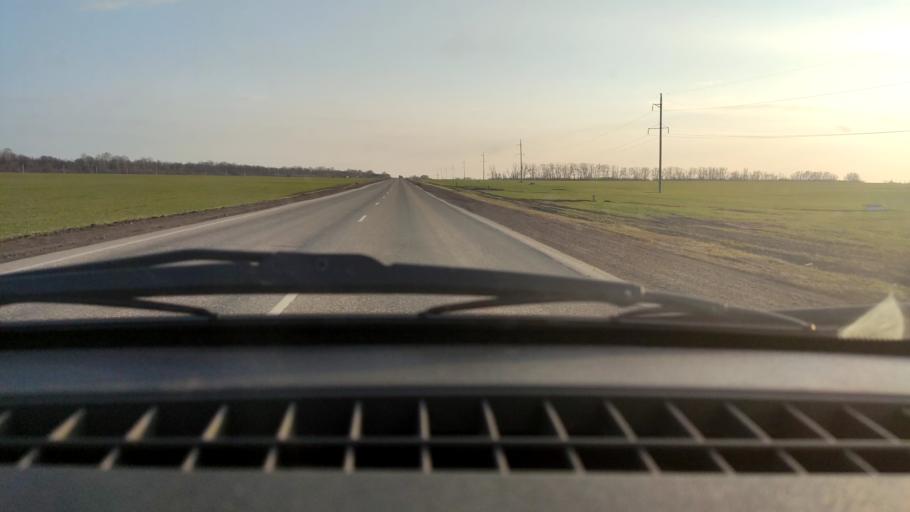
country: RU
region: Bashkortostan
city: Chishmy
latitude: 54.5578
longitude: 55.3397
